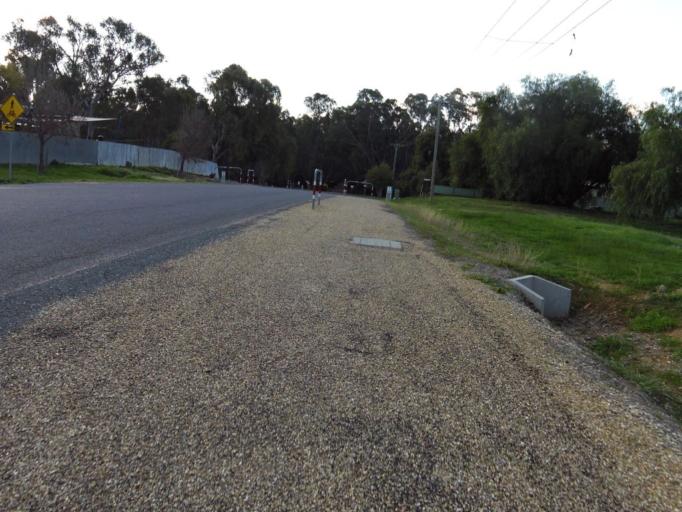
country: AU
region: New South Wales
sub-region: Corowa Shire
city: Corowa
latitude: -36.0111
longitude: 146.3989
